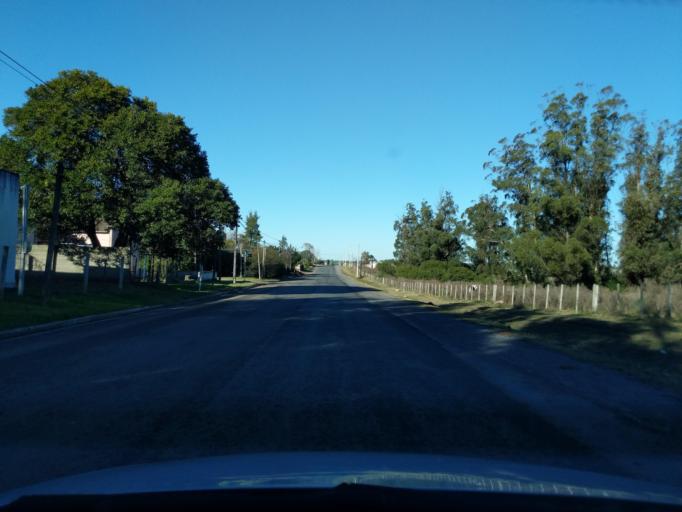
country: UY
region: Florida
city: Florida
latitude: -34.0946
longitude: -56.2400
